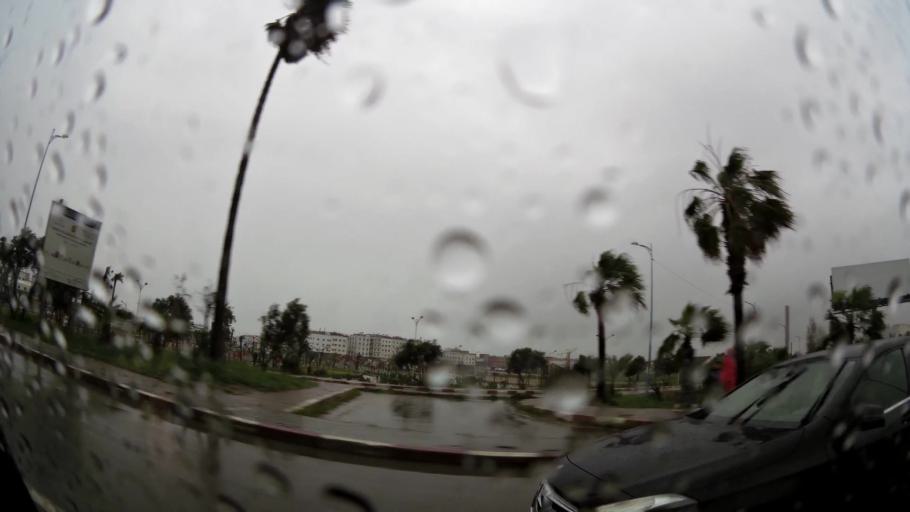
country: MA
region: Grand Casablanca
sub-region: Mediouna
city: Tit Mellil
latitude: 33.6011
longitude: -7.5084
